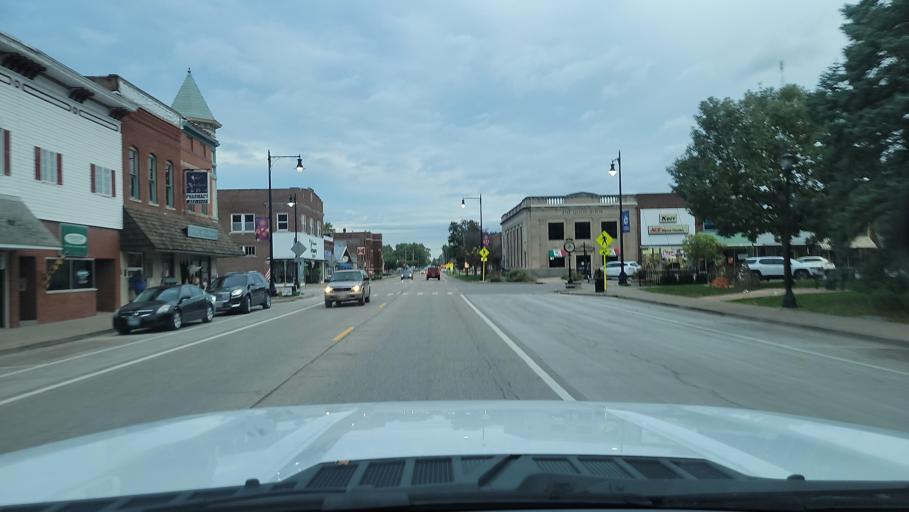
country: US
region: Illinois
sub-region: Schuyler County
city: Rushville
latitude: 40.1210
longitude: -90.5636
